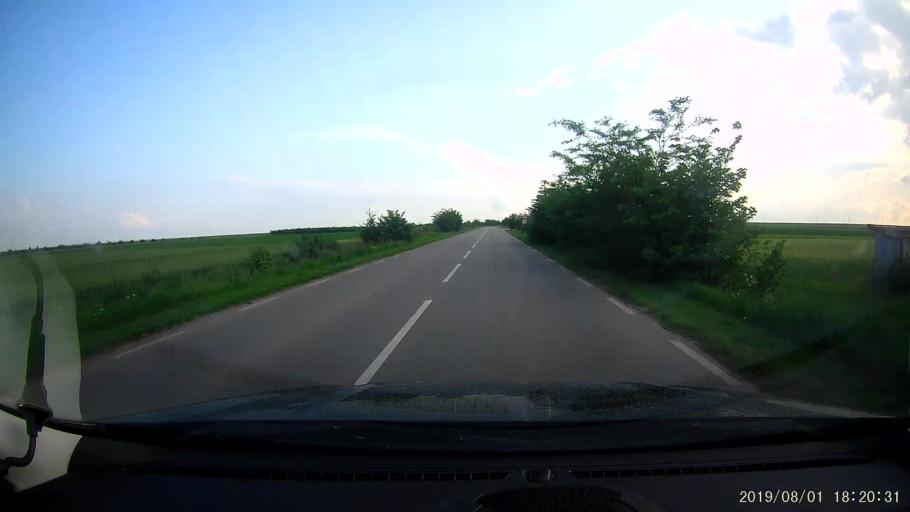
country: BG
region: Shumen
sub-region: Obshtina Kaolinovo
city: Kaolinovo
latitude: 43.6696
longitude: 27.0877
